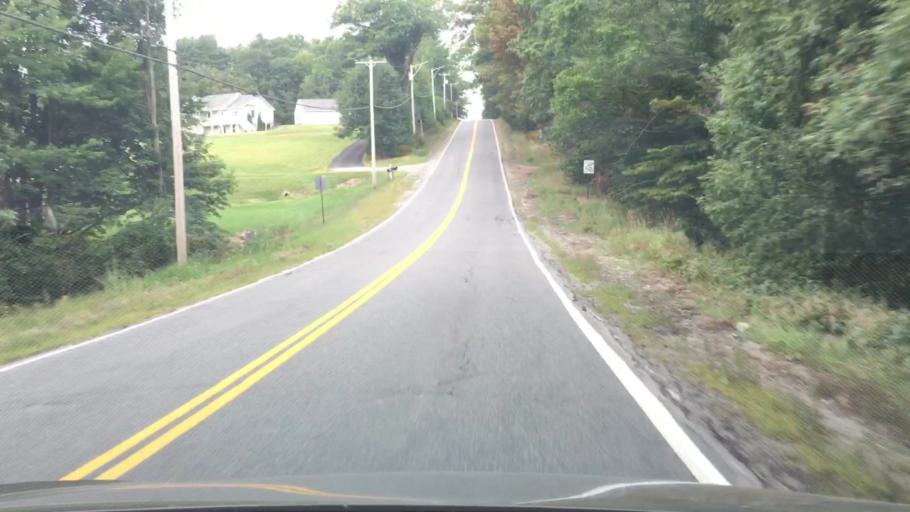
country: US
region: Maine
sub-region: Androscoggin County
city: Livermore
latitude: 44.3332
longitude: -70.2216
